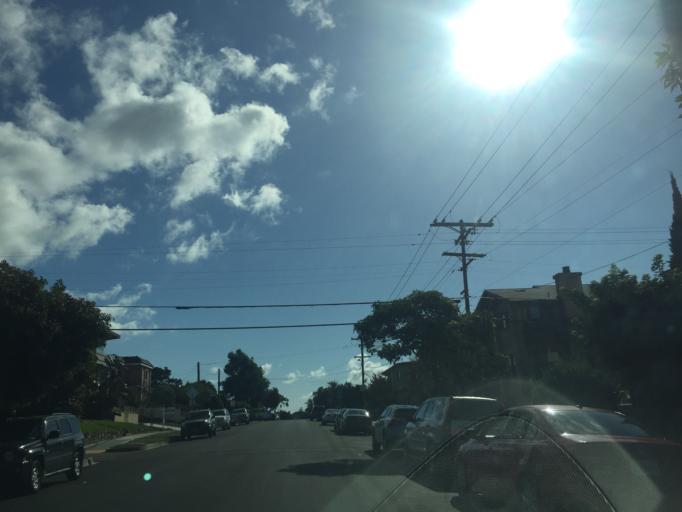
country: US
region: California
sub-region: San Diego County
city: La Jolla
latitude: 32.7944
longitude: -117.2412
